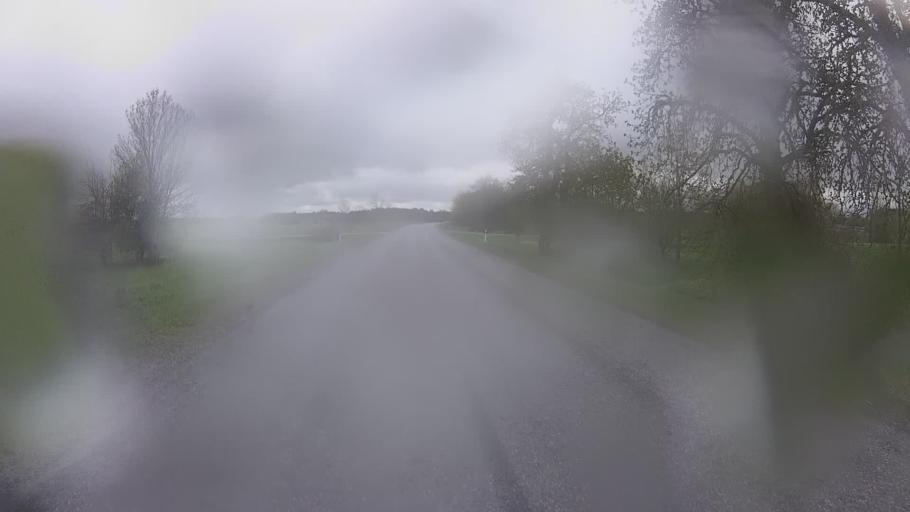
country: EE
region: Hiiumaa
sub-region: Kaerdla linn
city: Kardla
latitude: 58.8350
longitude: 22.8021
